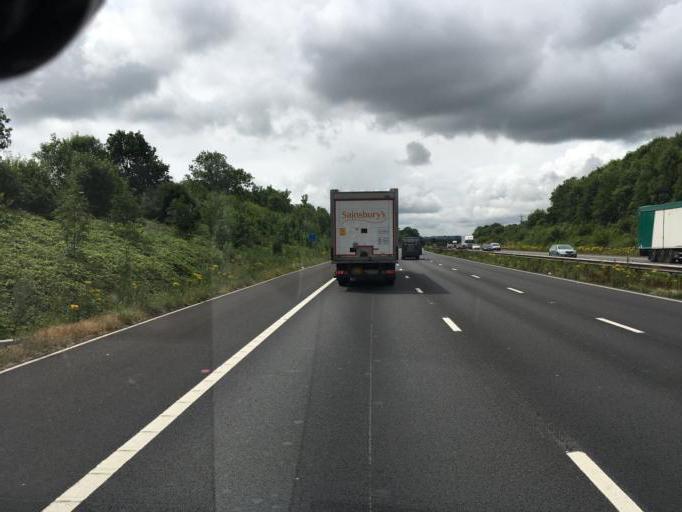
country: GB
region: England
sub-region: Gloucestershire
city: Stonehouse
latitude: 51.7679
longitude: -2.3134
